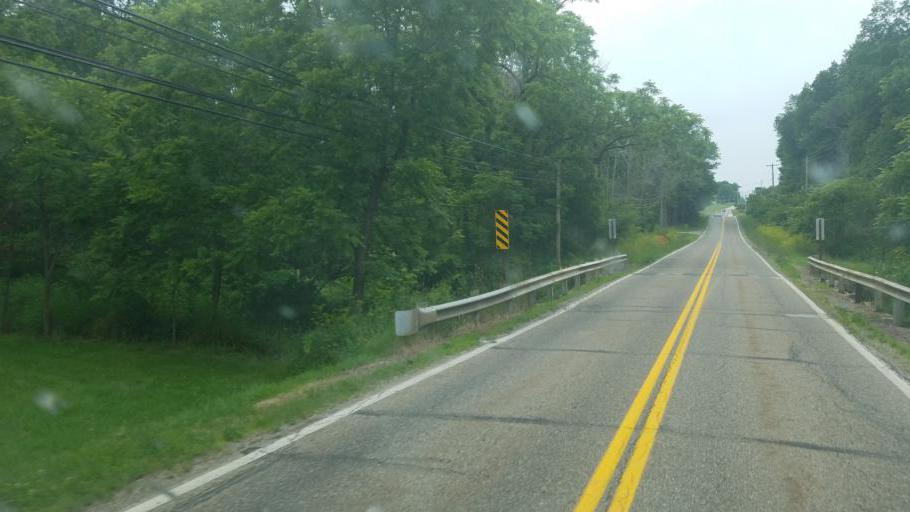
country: US
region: Ohio
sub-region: Portage County
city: Ravenna
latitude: 41.0984
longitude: -81.1872
